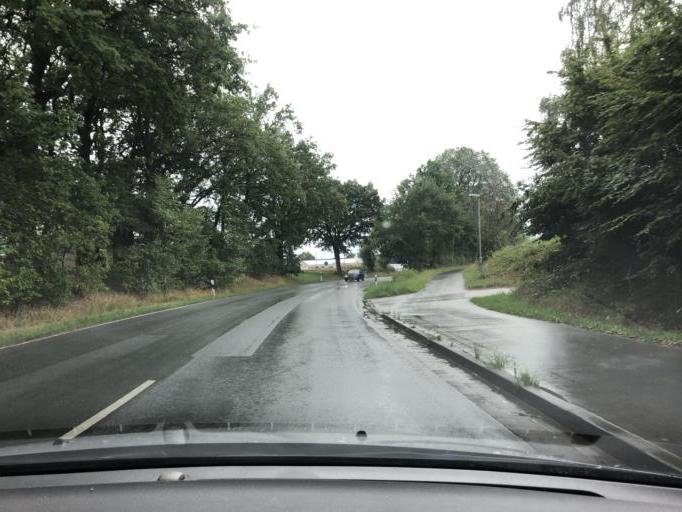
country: DE
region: North Rhine-Westphalia
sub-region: Regierungsbezirk Dusseldorf
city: Schermbeck
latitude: 51.7025
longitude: 6.8762
